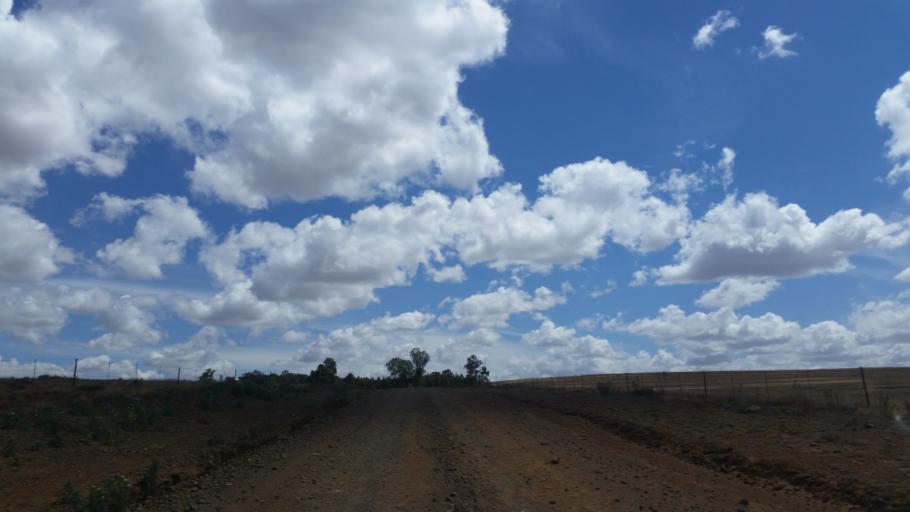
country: ZA
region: Orange Free State
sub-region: Thabo Mofutsanyana District Municipality
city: Bethlehem
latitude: -28.1918
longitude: 28.5869
